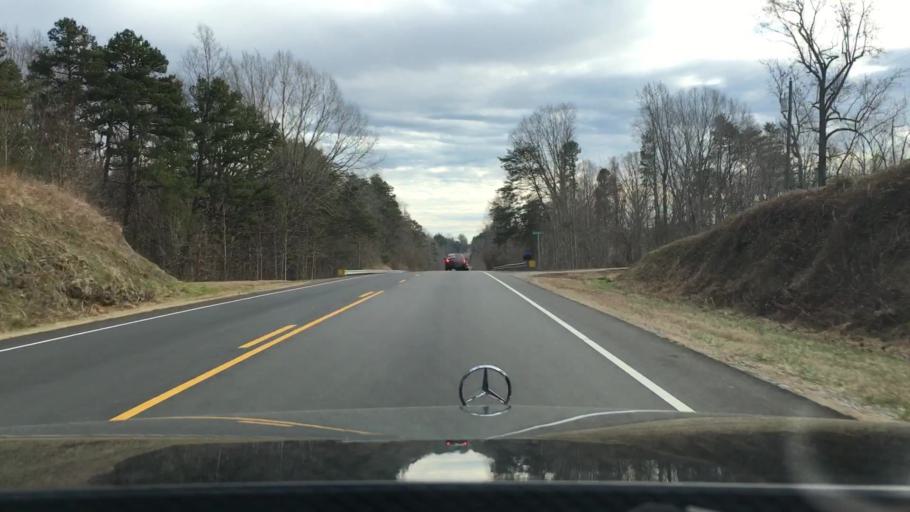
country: US
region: North Carolina
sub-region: Caswell County
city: Yanceyville
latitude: 36.4472
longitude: -79.3660
